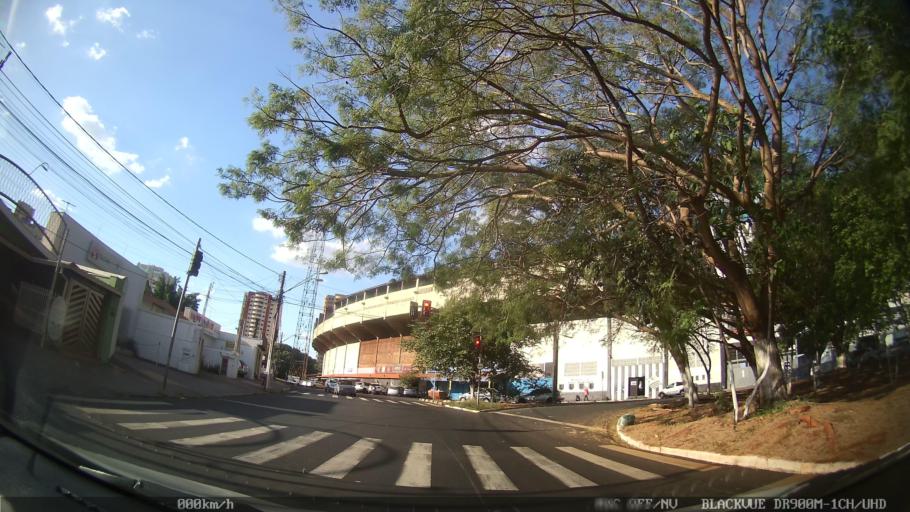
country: BR
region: Sao Paulo
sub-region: Ribeirao Preto
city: Ribeirao Preto
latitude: -21.1869
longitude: -47.7901
